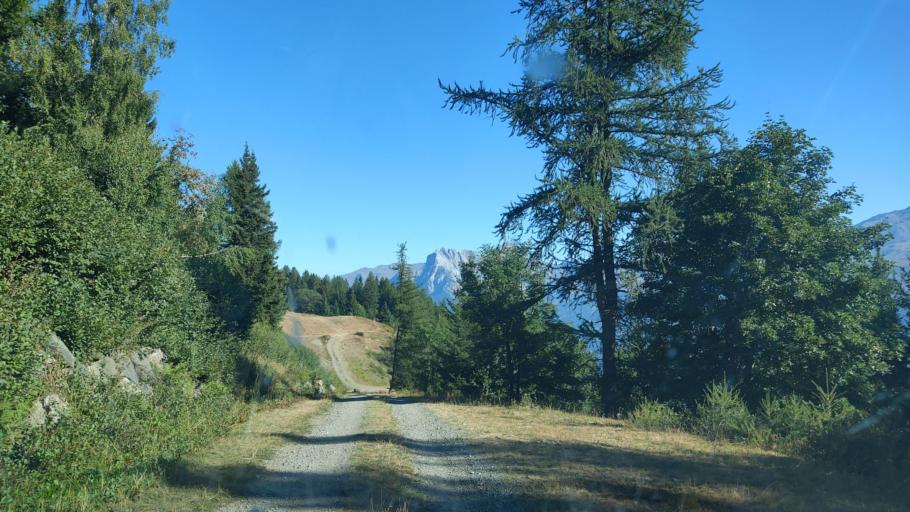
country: FR
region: Rhone-Alpes
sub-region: Departement de la Savoie
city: Saint-Michel-de-Maurienne
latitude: 45.1803
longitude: 6.4664
